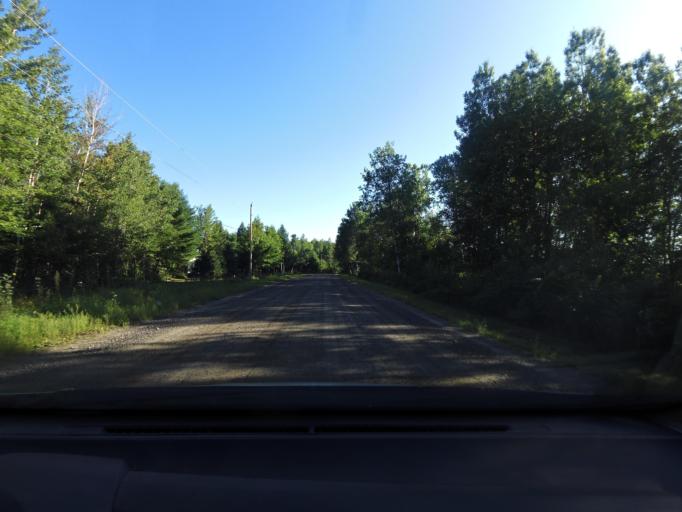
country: CA
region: Quebec
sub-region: Mauricie
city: Becancour
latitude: 46.5496
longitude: -72.3939
